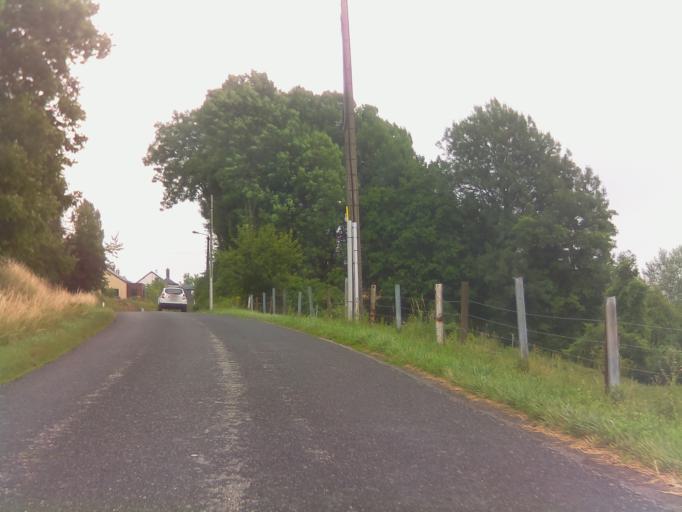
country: LU
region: Luxembourg
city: Eischen
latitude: 49.6479
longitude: 5.8601
